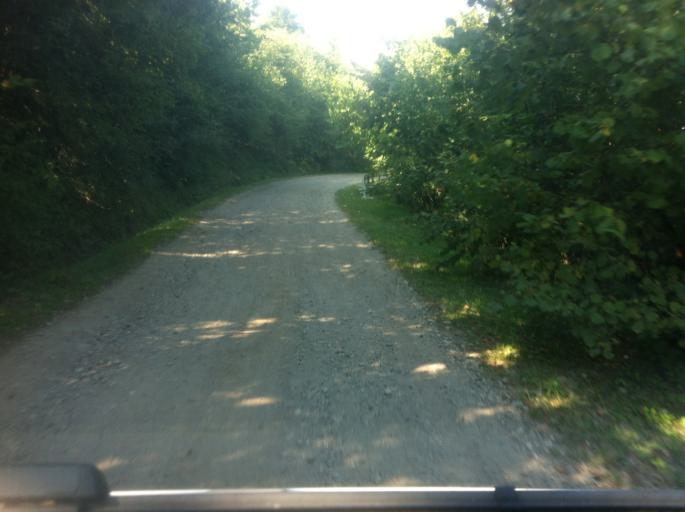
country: RO
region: Hunedoara
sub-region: Comuna Rau de Mori
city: Rau de Mori
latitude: 45.4541
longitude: 22.8966
